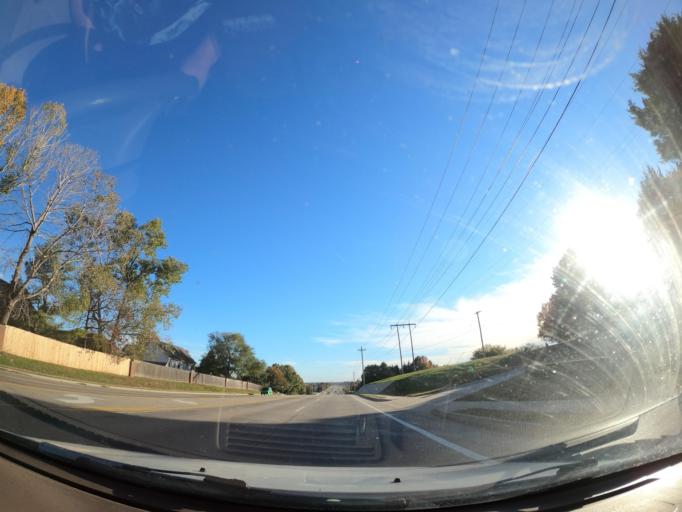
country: US
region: Oklahoma
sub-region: Tulsa County
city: Owasso
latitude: 36.2882
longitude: -95.8301
